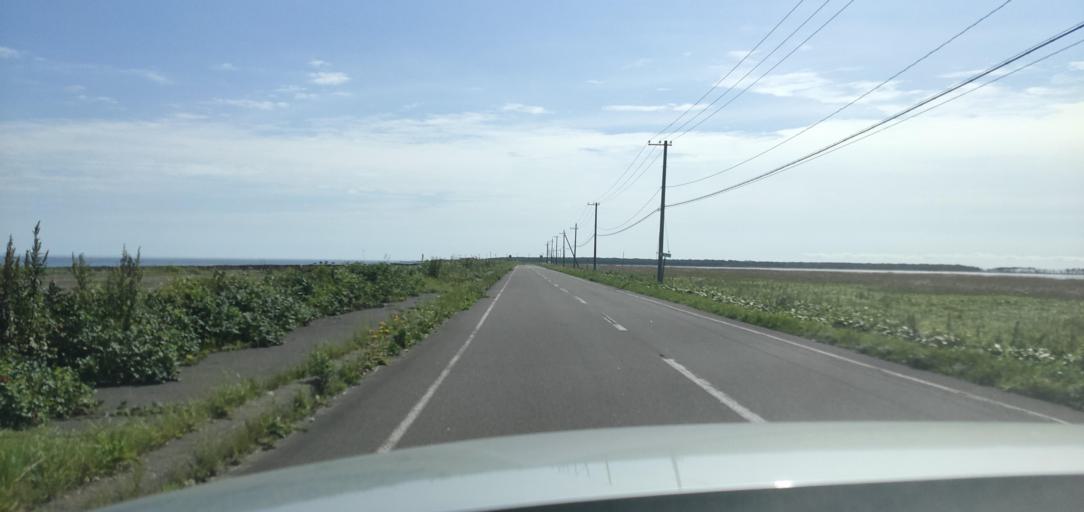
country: JP
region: Hokkaido
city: Shibetsu
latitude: 43.6157
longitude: 145.2405
